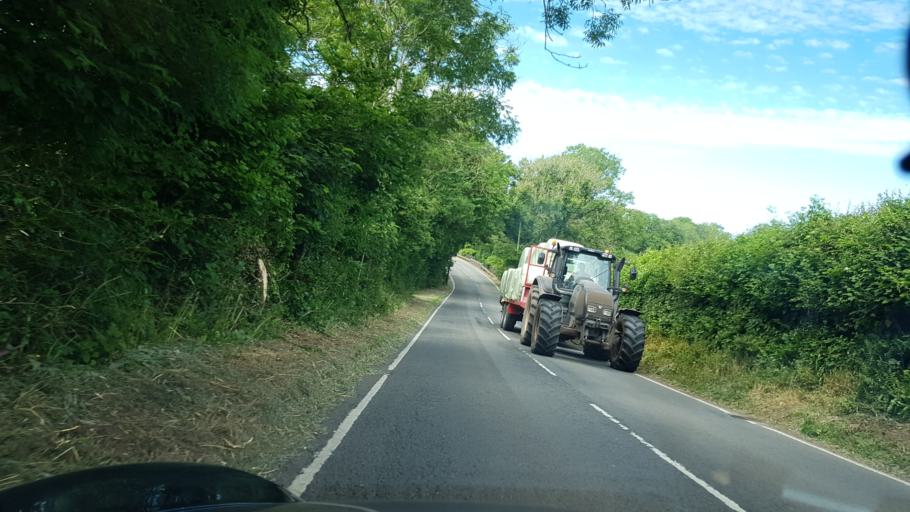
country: GB
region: Wales
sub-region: Carmarthenshire
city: Whitland
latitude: 51.7805
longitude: -4.6261
